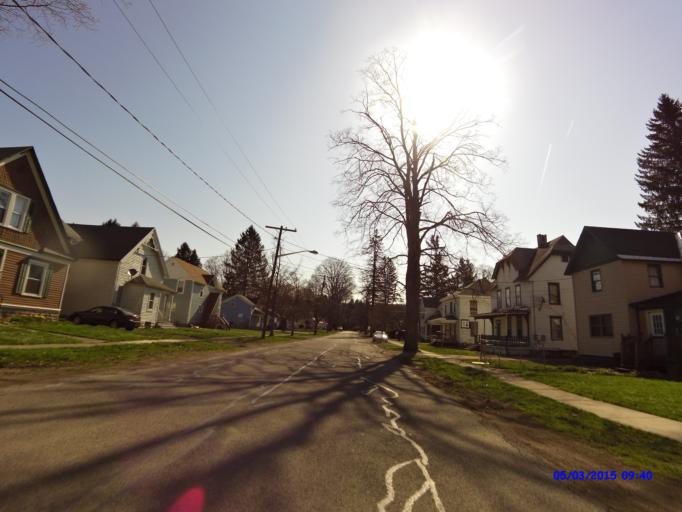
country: US
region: New York
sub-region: Cattaraugus County
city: Franklinville
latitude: 42.3358
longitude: -78.4550
